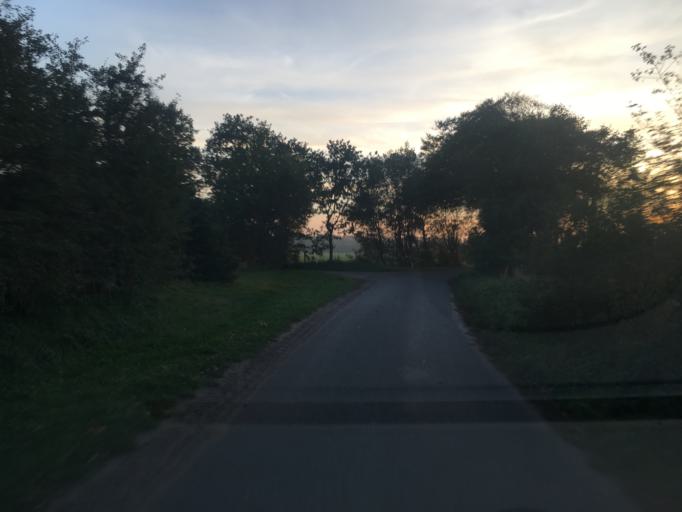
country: DE
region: Schleswig-Holstein
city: Bramstedtlund
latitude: 54.9893
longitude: 9.1001
